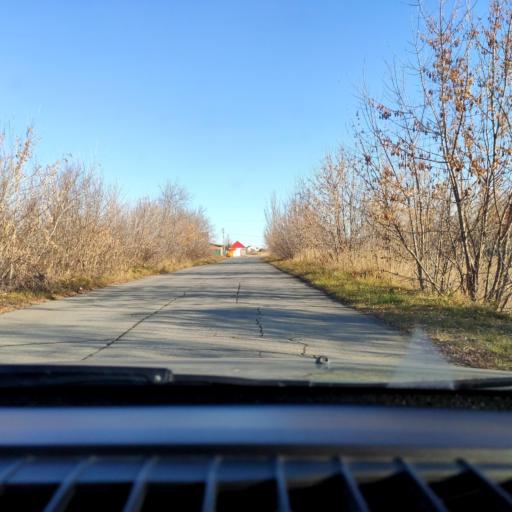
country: RU
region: Samara
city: Tol'yatti
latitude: 53.6632
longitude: 49.3359
